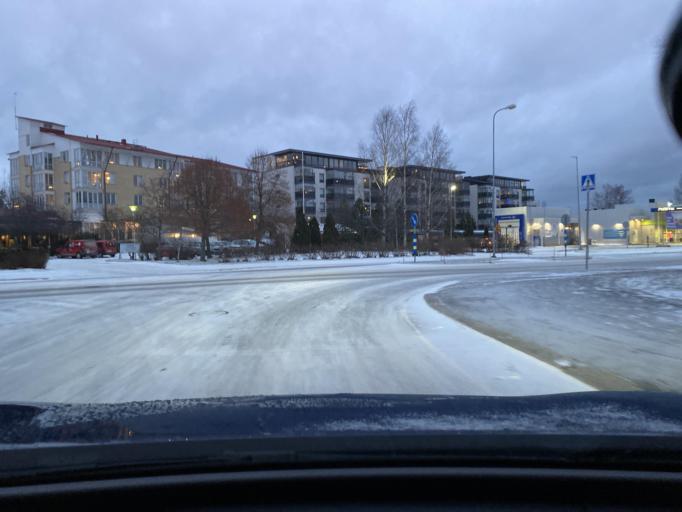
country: FI
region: Satakunta
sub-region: Rauma
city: Rauma
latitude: 61.1327
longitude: 21.5011
